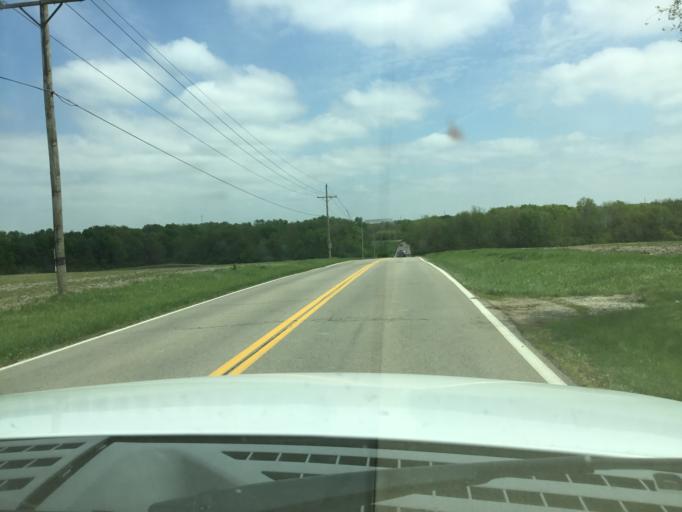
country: US
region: Kansas
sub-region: Shawnee County
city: Topeka
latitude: 38.9860
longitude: -95.7144
